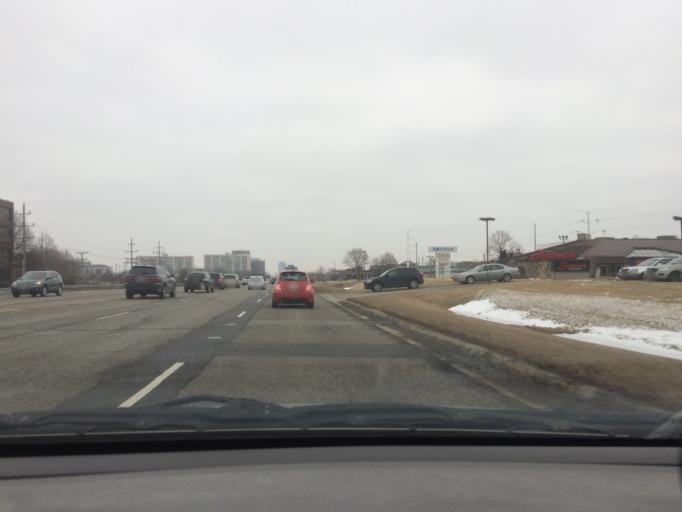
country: US
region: Illinois
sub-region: DuPage County
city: Downers Grove
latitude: 41.8398
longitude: -87.9984
